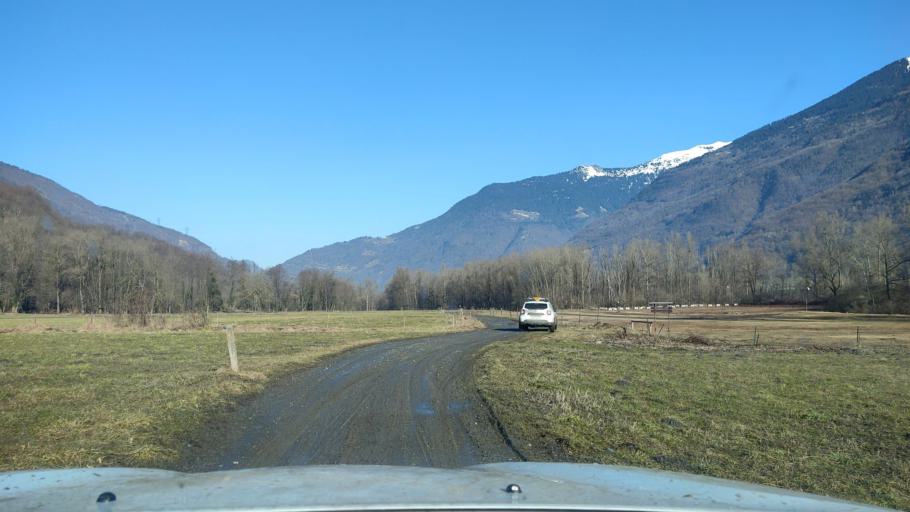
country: FR
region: Rhone-Alpes
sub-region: Departement de la Savoie
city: La Bathie
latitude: 45.6112
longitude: 6.4466
